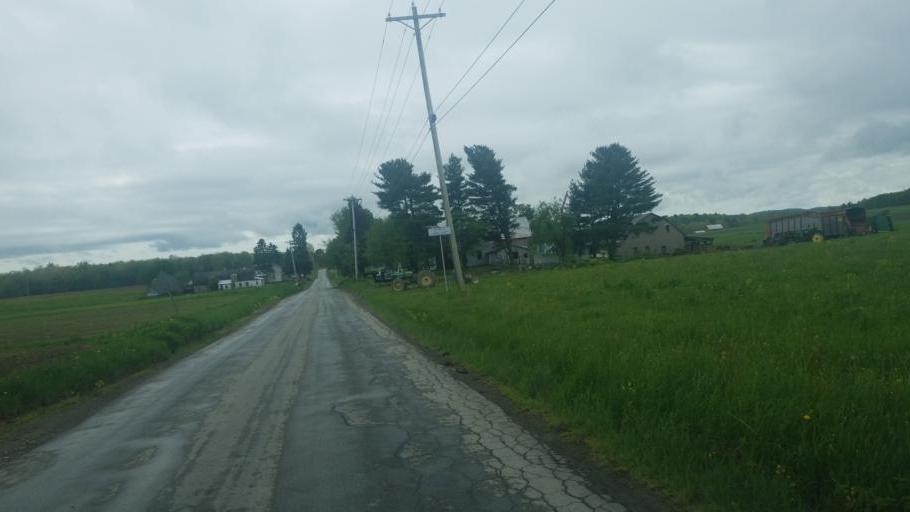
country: US
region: Pennsylvania
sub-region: Forest County
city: Tionesta
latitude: 41.4053
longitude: -79.3880
